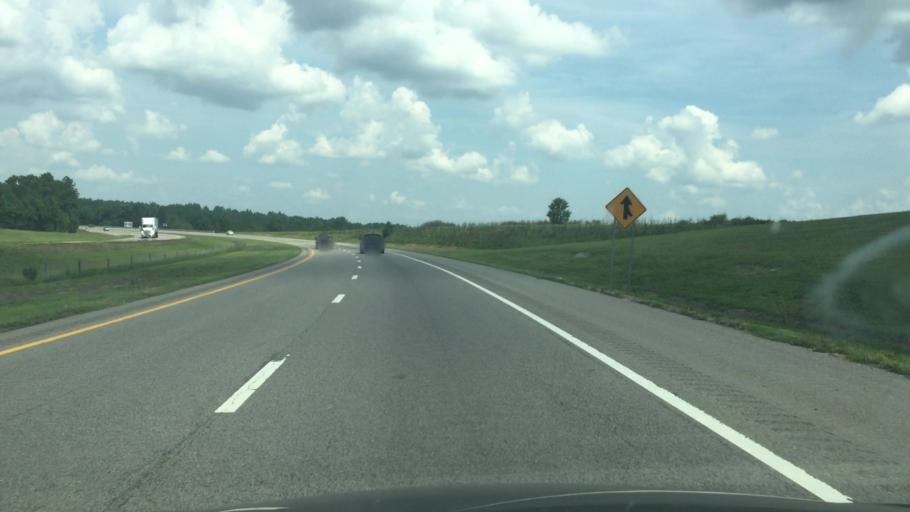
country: US
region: North Carolina
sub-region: Richmond County
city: Ellerbe
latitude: 35.1746
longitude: -79.7131
